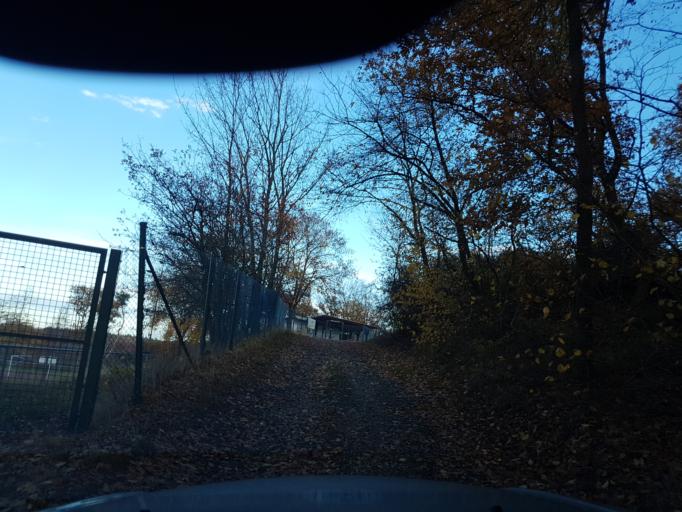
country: DE
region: Hesse
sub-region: Regierungsbezirk Darmstadt
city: Bad Schwalbach
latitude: 50.1242
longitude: 8.0175
